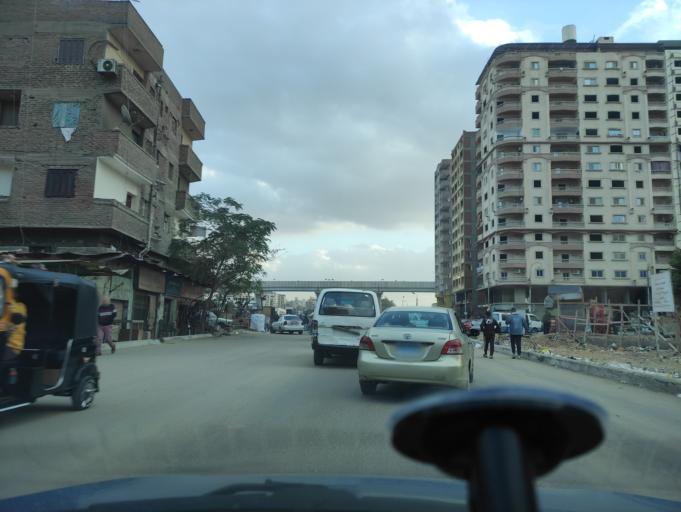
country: EG
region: Muhafazat al Qalyubiyah
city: Al Khankah
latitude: 30.1303
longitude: 31.3612
